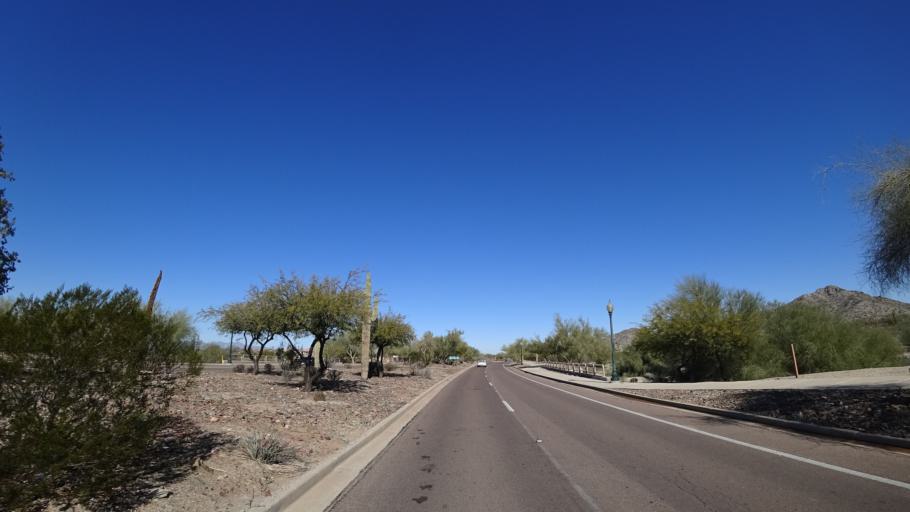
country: US
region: Arizona
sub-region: Maricopa County
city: Goodyear
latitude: 33.3339
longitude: -112.4249
